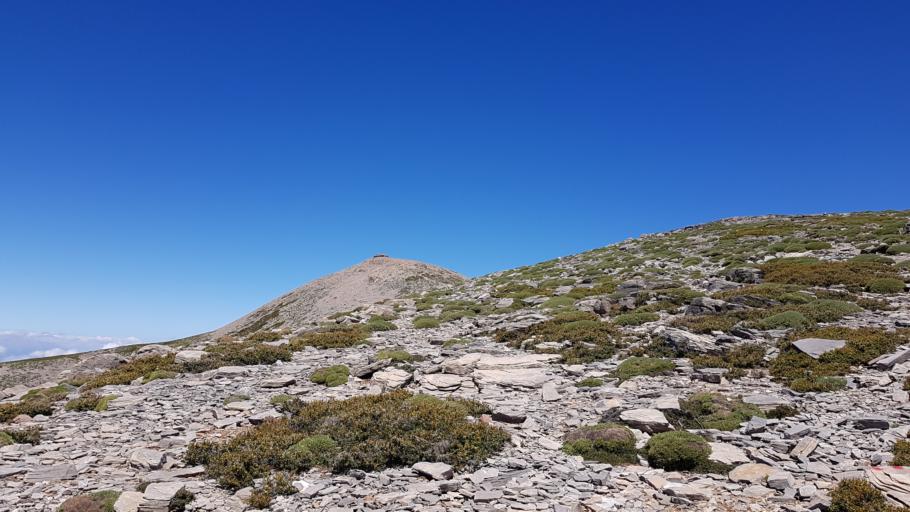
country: GR
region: Crete
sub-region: Nomos Rethymnis
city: Zoniana
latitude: 35.2233
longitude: 24.7757
